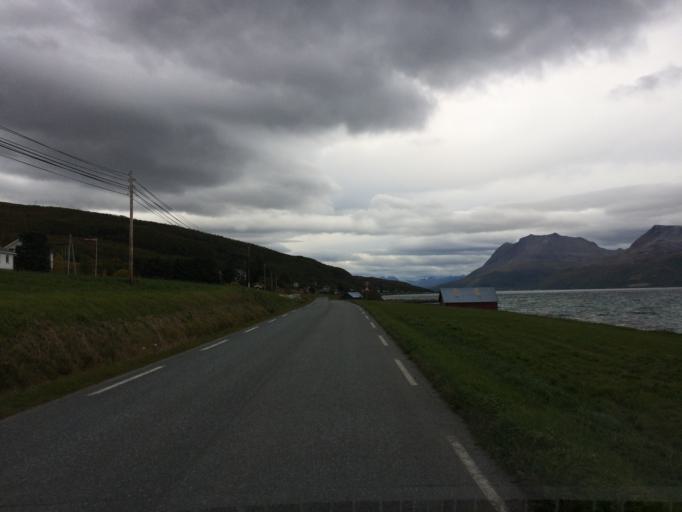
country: NO
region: Troms
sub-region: Sorreisa
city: Sorreisa
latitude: 69.5290
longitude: 18.2924
